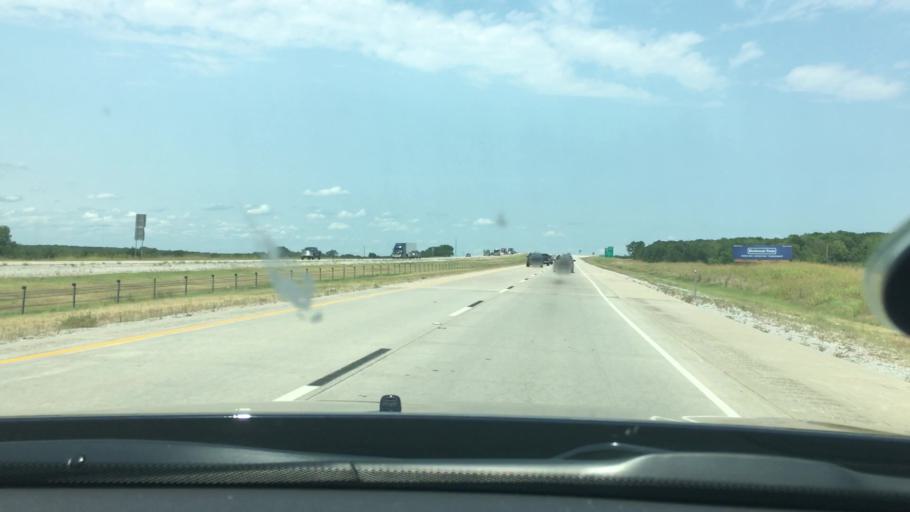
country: US
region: Oklahoma
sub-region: Carter County
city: Ardmore
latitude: 34.1298
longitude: -97.1562
